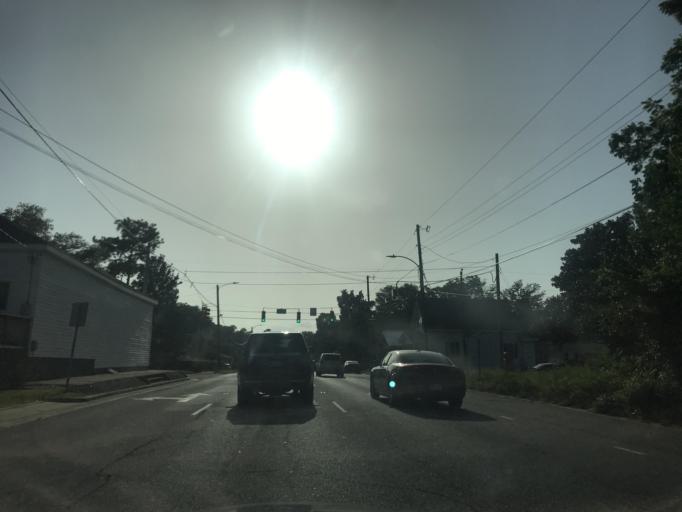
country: US
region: North Carolina
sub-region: New Hanover County
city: Wilmington
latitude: 34.2260
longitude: -77.9376
